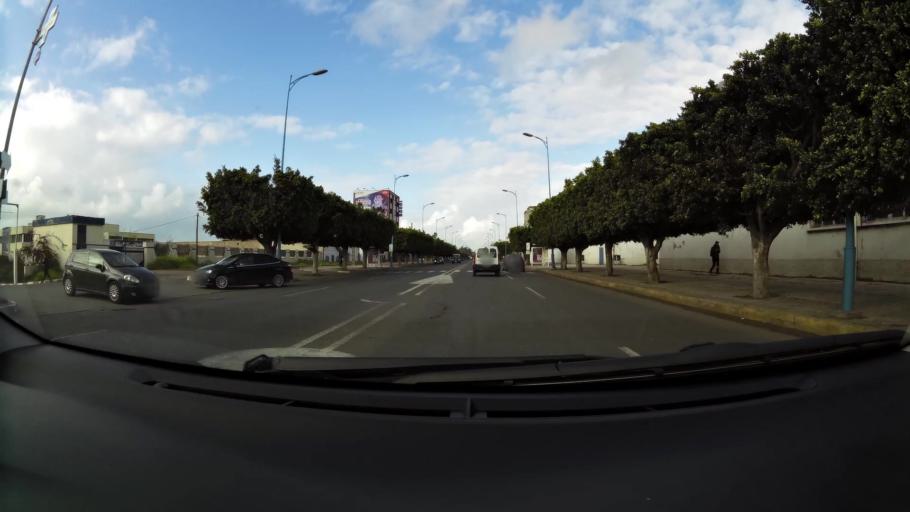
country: MA
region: Grand Casablanca
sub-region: Mohammedia
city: Mohammedia
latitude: 33.6879
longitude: -7.3991
